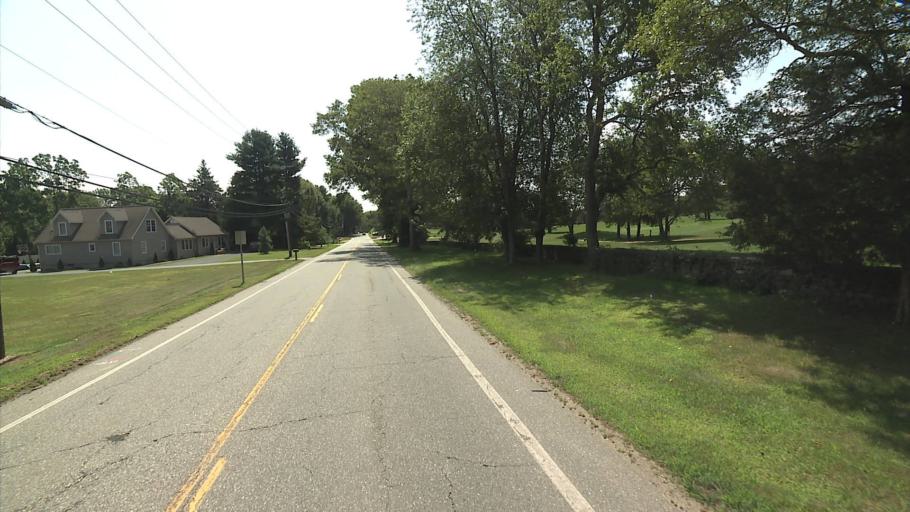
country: US
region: Connecticut
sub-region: New London County
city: Niantic
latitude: 41.3829
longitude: -72.2192
